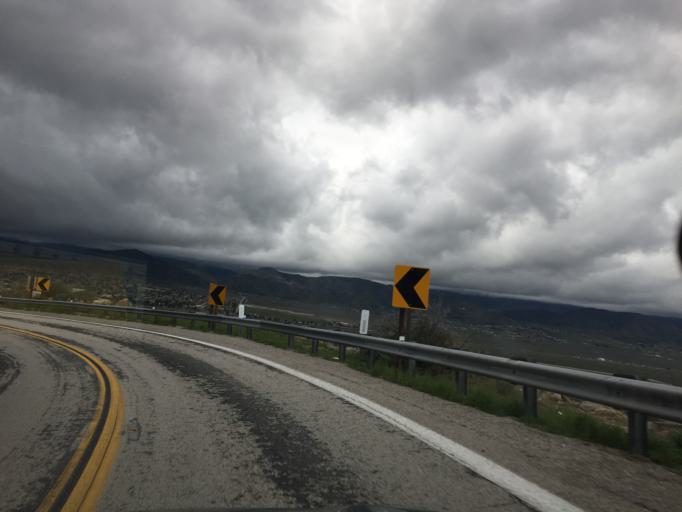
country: US
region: California
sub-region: Riverside County
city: Banning
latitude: 33.9037
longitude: -116.8584
